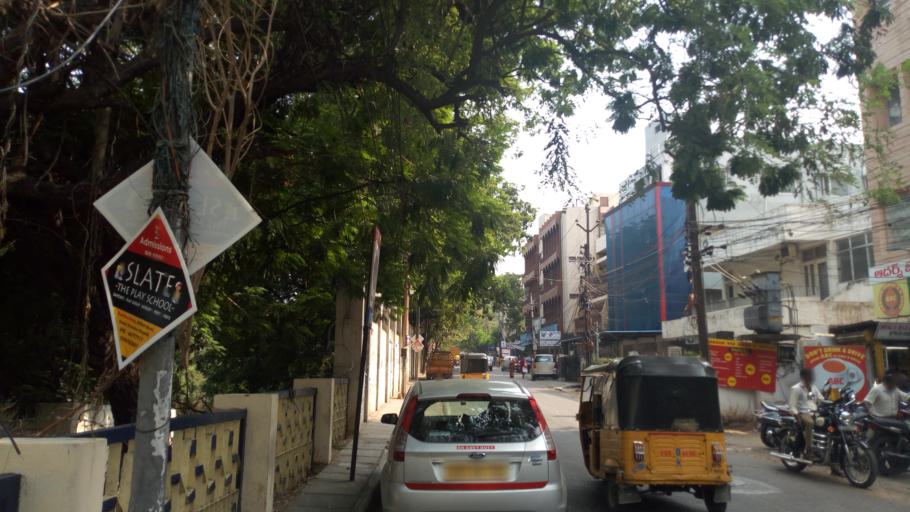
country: IN
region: Telangana
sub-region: Hyderabad
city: Hyderabad
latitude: 17.4060
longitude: 78.4730
